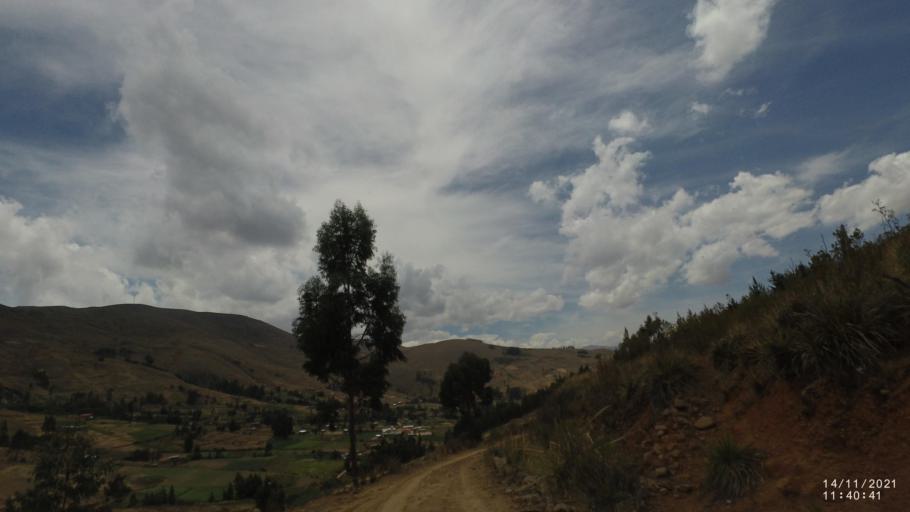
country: BO
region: Cochabamba
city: Colomi
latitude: -17.3517
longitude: -65.9954
